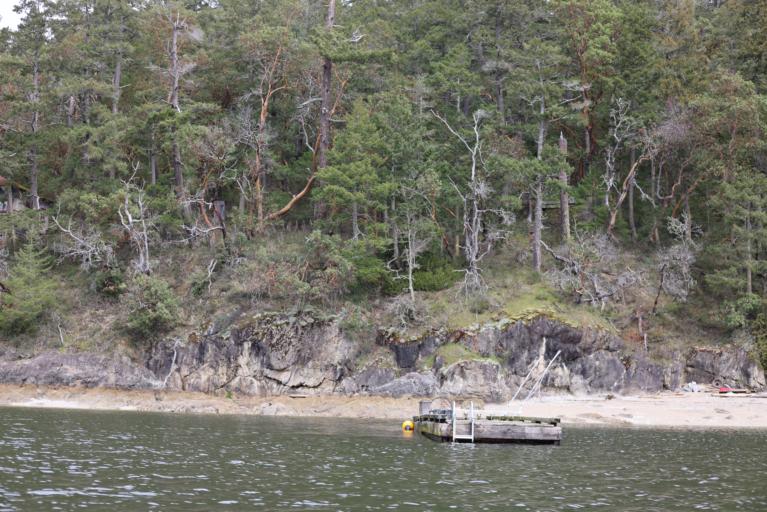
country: CA
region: British Columbia
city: North Saanich
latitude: 48.5936
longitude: -123.4717
